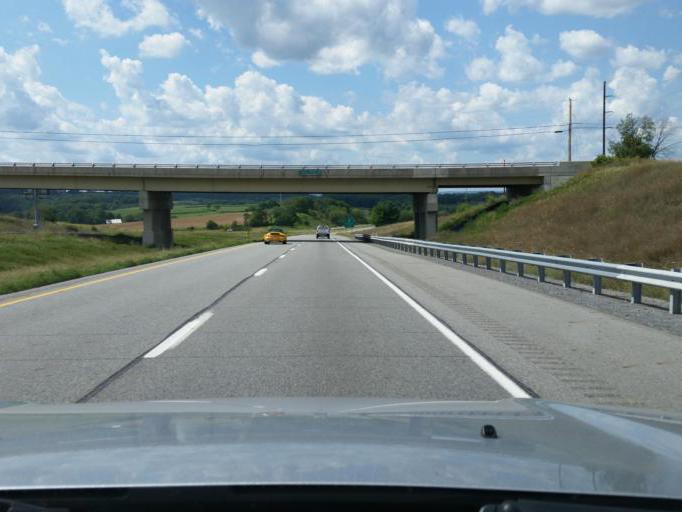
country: US
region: Pennsylvania
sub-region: Bedford County
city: Bedford
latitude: 40.0751
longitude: -78.5230
